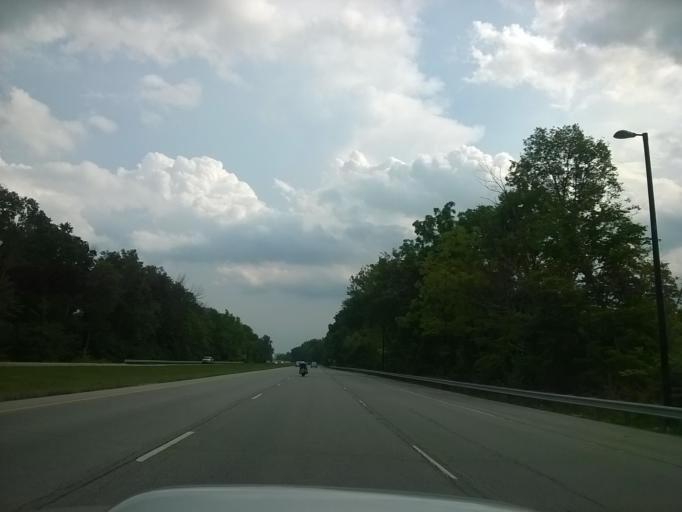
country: US
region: Indiana
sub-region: Hamilton County
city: Carmel
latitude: 39.9525
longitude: -86.1140
